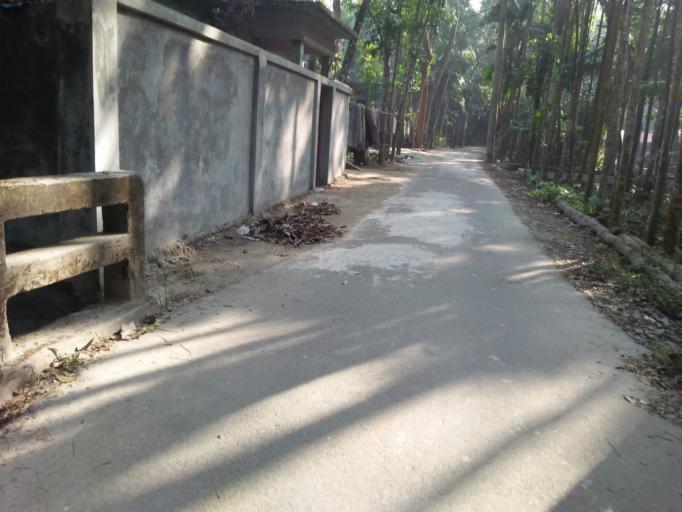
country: BD
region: Barisal
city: Bhola
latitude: 22.6764
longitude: 90.6384
